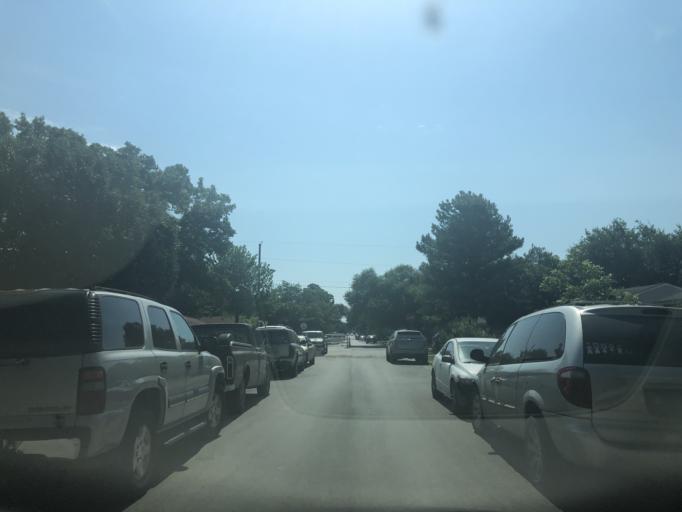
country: US
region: Texas
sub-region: Dallas County
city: Grand Prairie
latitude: 32.7166
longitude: -96.9994
